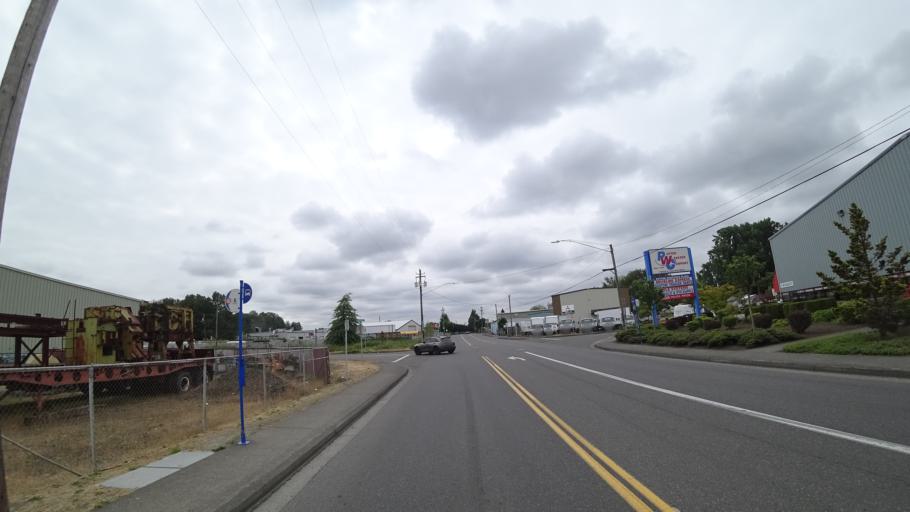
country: US
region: Washington
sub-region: Clark County
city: Vancouver
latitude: 45.5939
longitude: -122.6658
